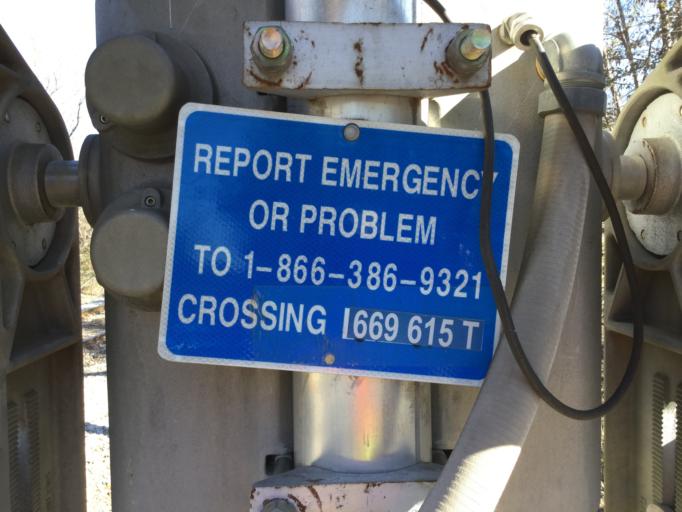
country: US
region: Kansas
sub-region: Montgomery County
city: Cherryvale
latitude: 37.2722
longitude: -95.5465
